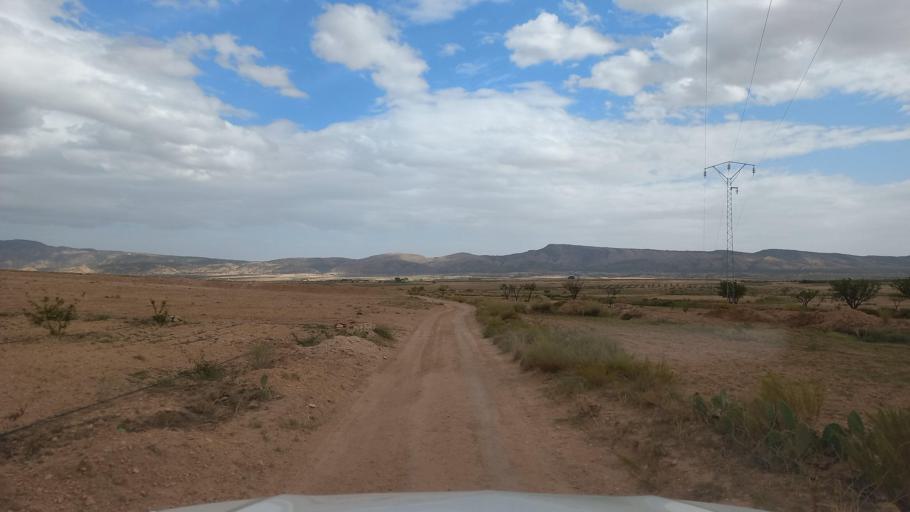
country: TN
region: Al Qasrayn
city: Sbiba
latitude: 35.3837
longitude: 9.1052
